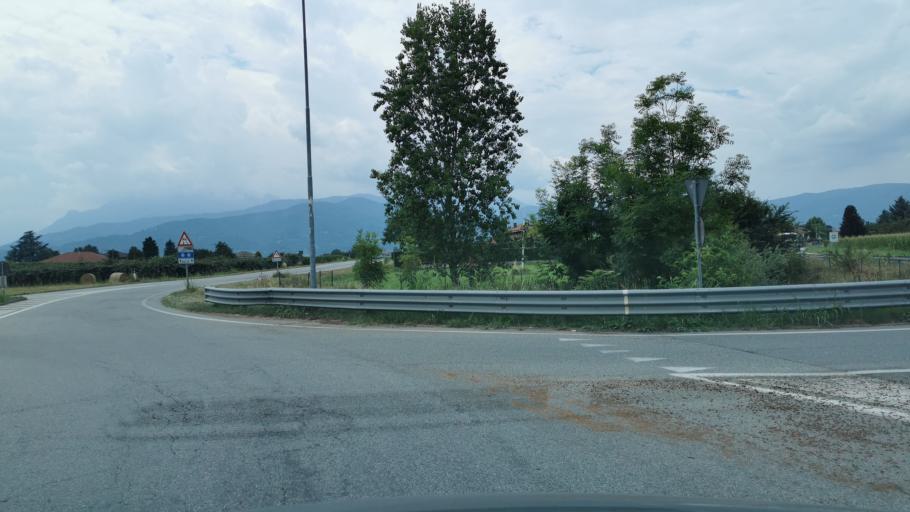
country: IT
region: Piedmont
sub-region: Provincia di Torino
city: Osasco
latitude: 44.8435
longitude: 7.3514
